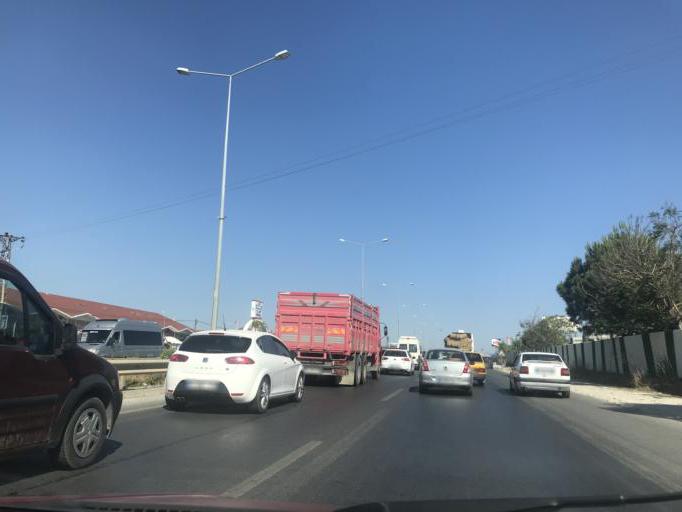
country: TR
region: Antalya
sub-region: Manavgat
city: Side
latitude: 36.8064
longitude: 31.3878
